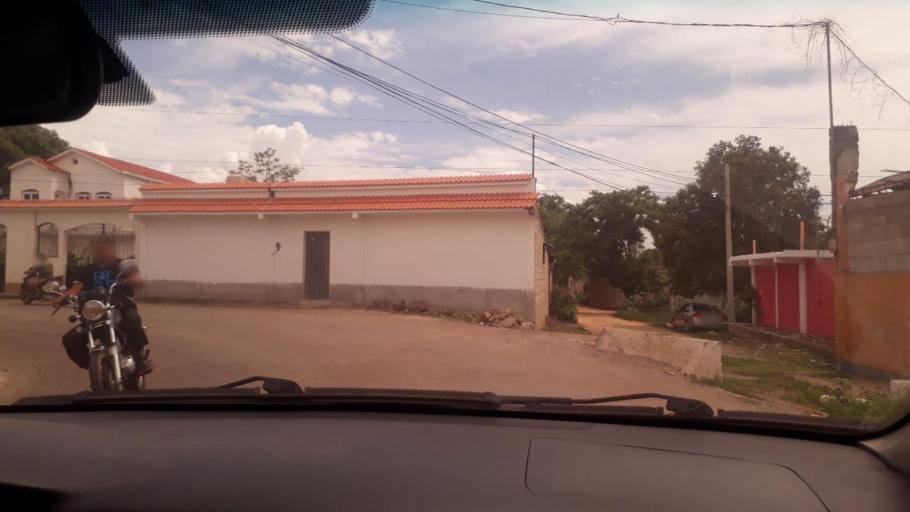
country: GT
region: Jutiapa
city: Jutiapa
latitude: 14.2865
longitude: -89.9119
